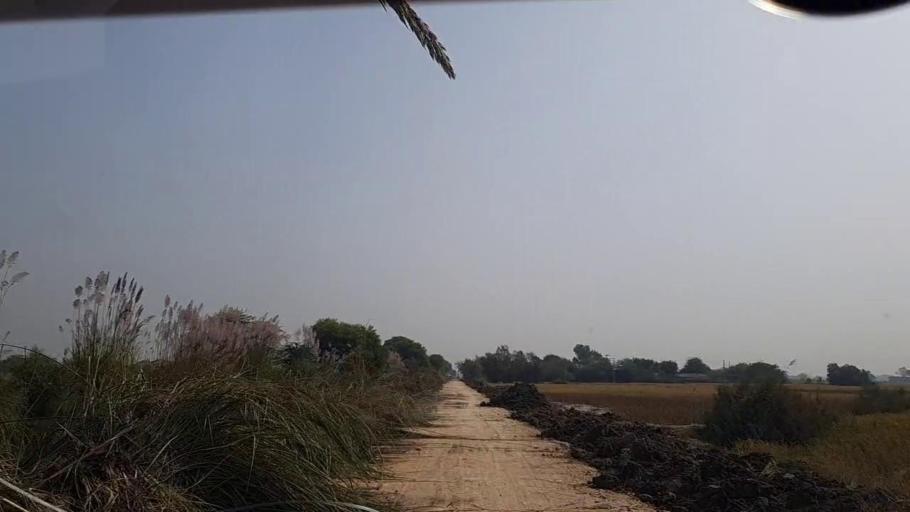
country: PK
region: Sindh
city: Shikarpur
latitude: 27.9201
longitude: 68.5808
